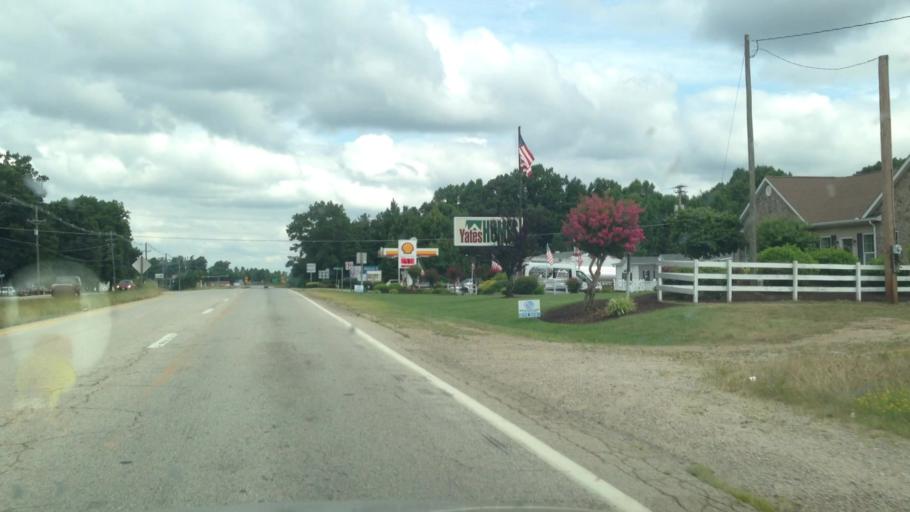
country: US
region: Virginia
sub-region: Pittsylvania County
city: Mount Hermon
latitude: 36.6917
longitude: -79.3671
